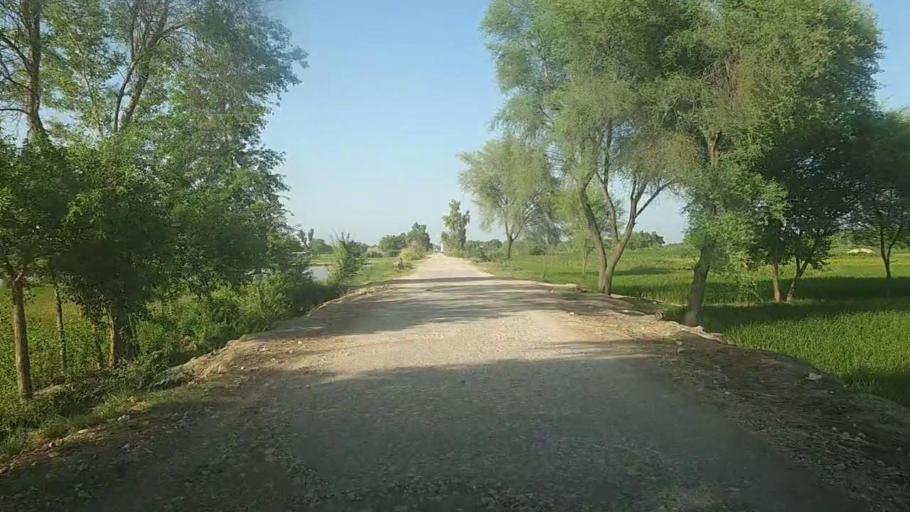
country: PK
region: Sindh
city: Khairpur
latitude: 28.1055
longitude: 69.6333
